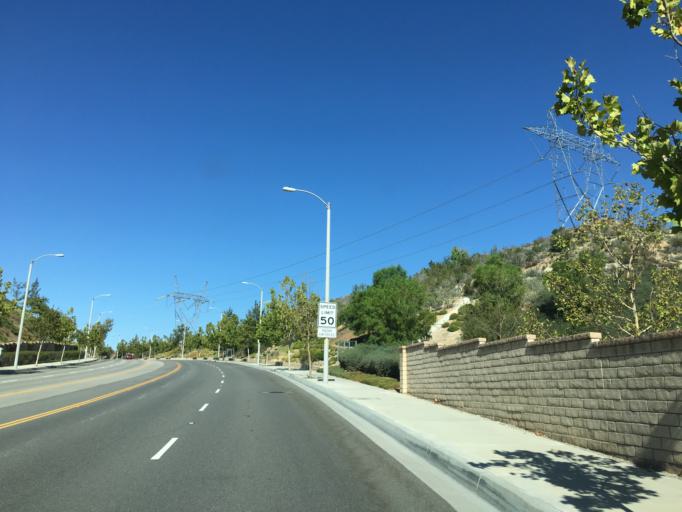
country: US
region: California
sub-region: Los Angeles County
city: Santa Clarita
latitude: 34.4430
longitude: -118.4902
